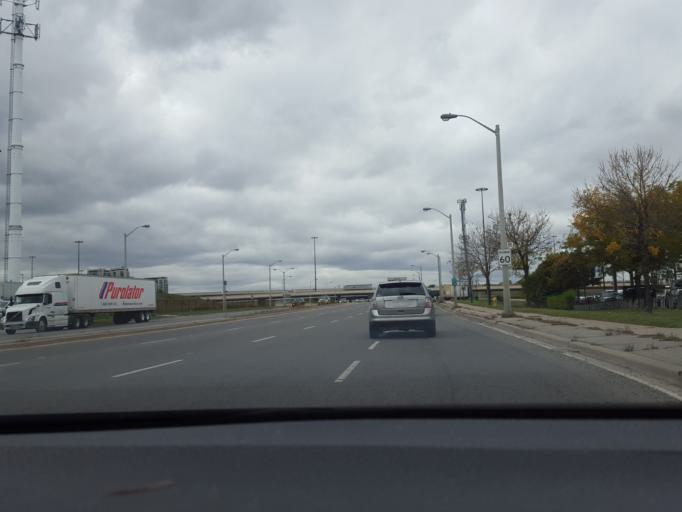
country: CA
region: Ontario
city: Etobicoke
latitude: 43.6165
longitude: -79.5466
